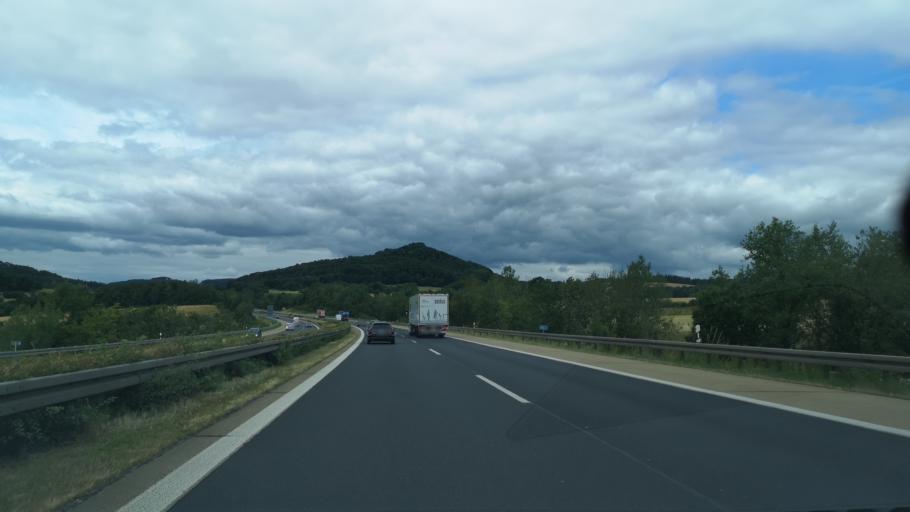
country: DE
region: Bavaria
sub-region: Regierungsbezirk Unterfranken
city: Schondra
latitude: 50.2749
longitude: 9.8763
